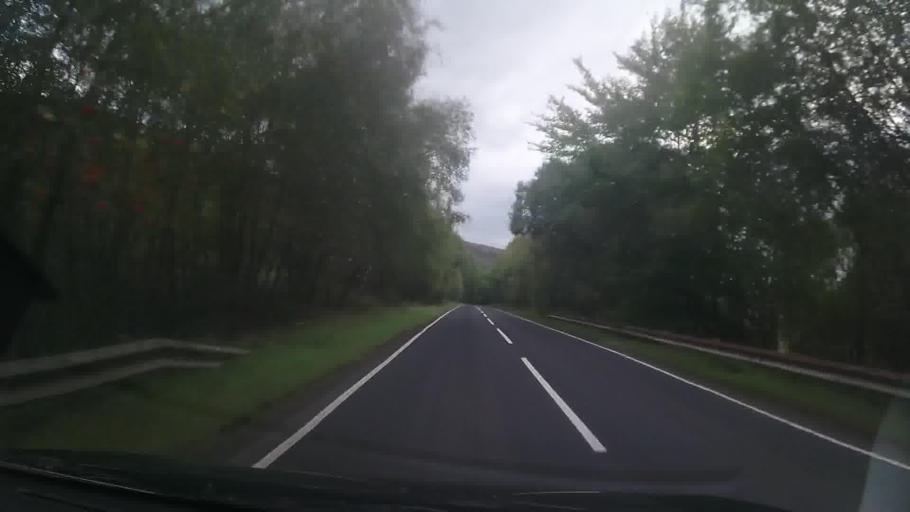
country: GB
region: Scotland
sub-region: Argyll and Bute
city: Garelochhead
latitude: 56.2280
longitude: -4.9802
